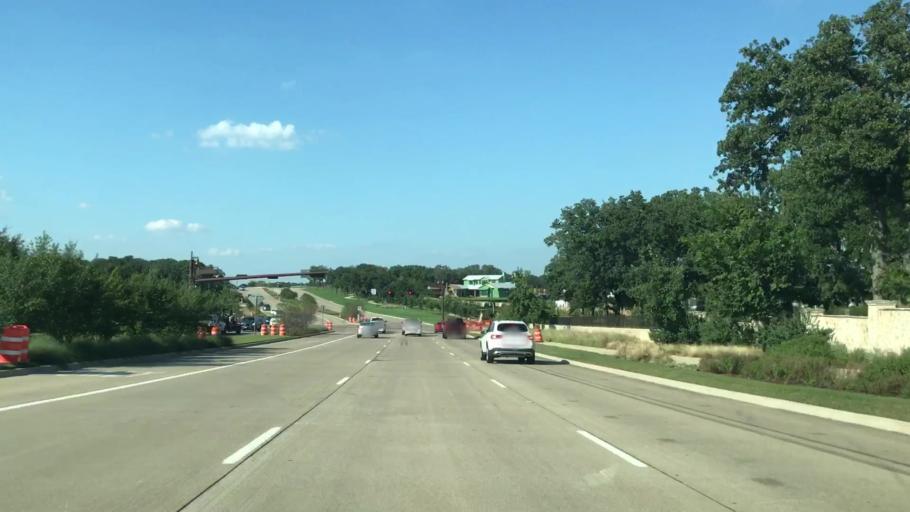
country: US
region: Texas
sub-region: Denton County
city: Trophy Club
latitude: 32.9770
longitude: -97.1857
